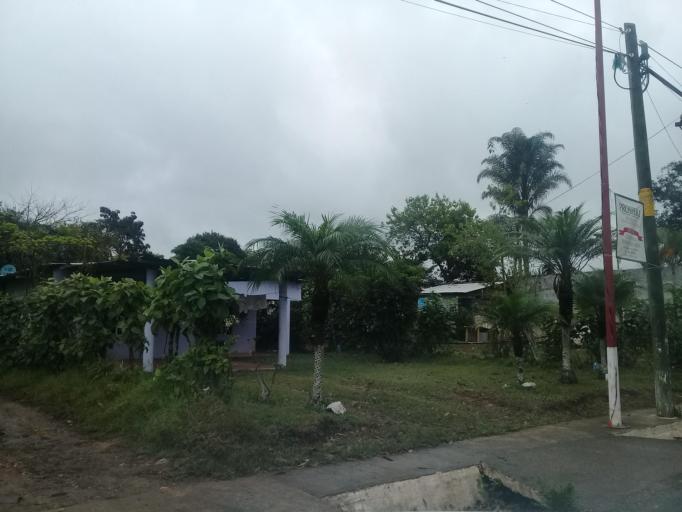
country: MX
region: Veracruz
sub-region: Amatlan de los Reyes
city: Trapiche Viejo
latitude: 18.8308
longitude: -96.9558
